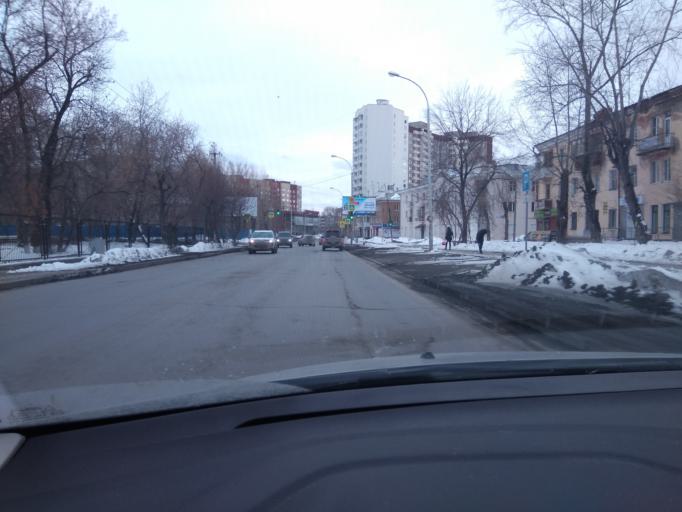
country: RU
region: Sverdlovsk
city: Yekaterinburg
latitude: 56.8609
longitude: 60.6323
